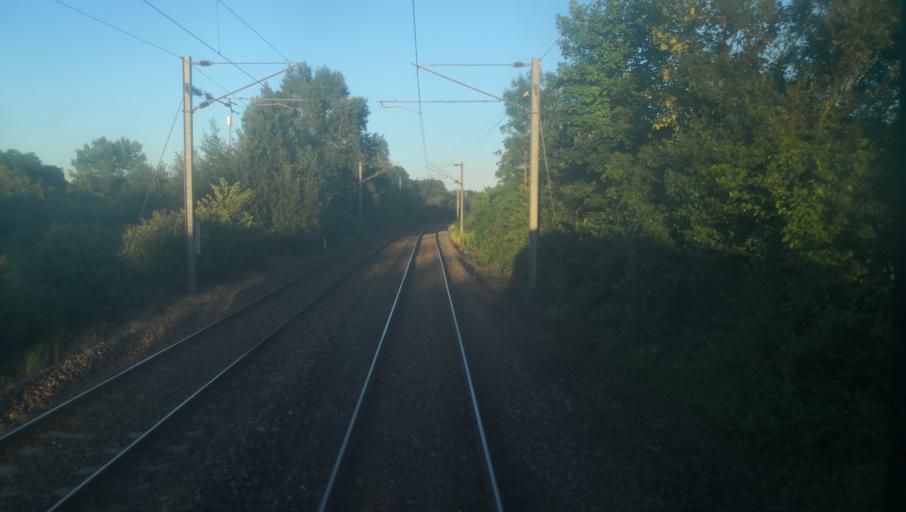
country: FR
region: Bourgogne
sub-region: Departement de la Nievre
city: Varennes-Vauzelles
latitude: 47.0003
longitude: 3.1387
